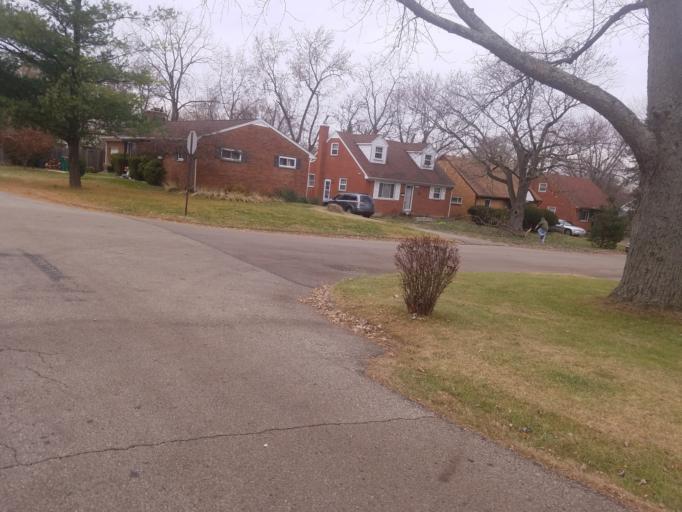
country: US
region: Ohio
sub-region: Montgomery County
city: Kettering
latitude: 39.7084
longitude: -84.1550
